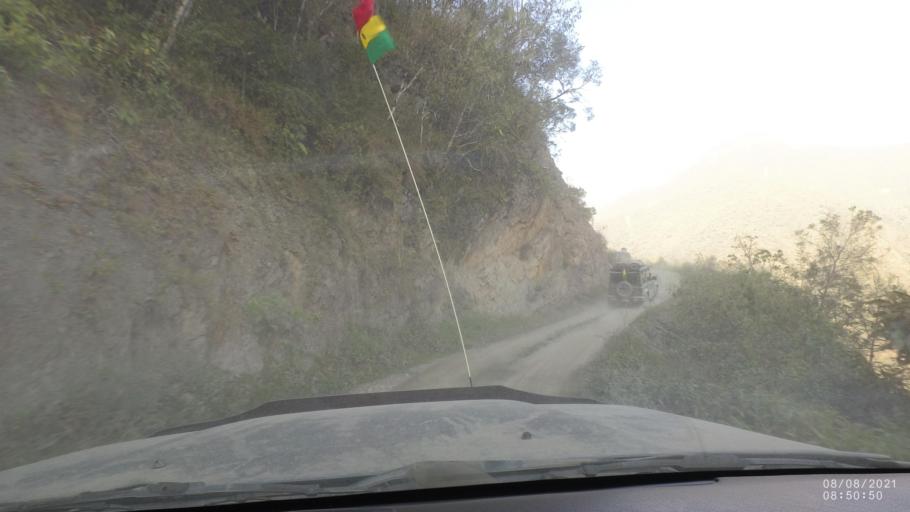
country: BO
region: La Paz
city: Quime
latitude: -16.5364
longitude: -66.7599
